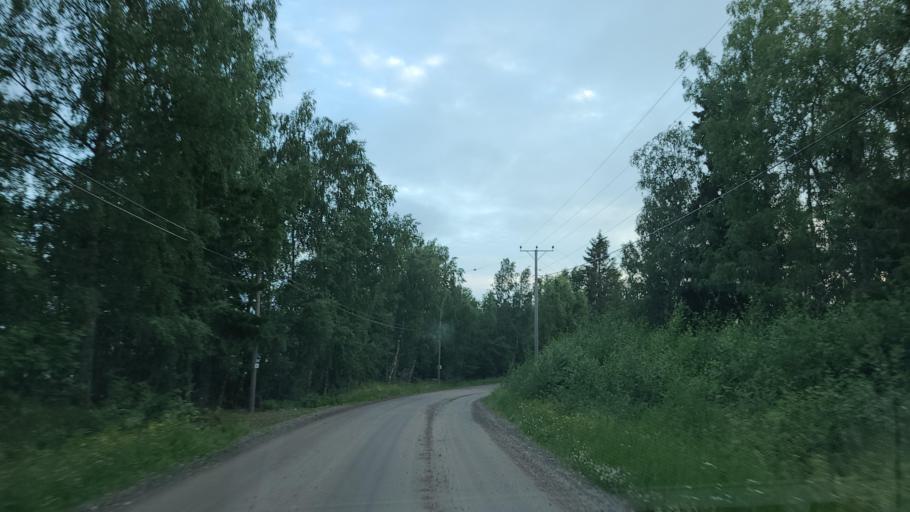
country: FI
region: Ostrobothnia
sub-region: Vaasa
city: Replot
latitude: 63.2956
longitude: 21.1186
